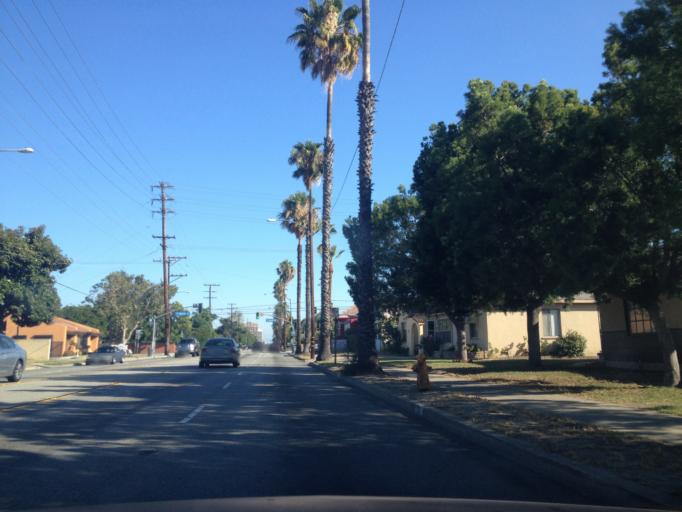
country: US
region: California
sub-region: Orange County
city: Anaheim
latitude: 33.8439
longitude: -117.9228
